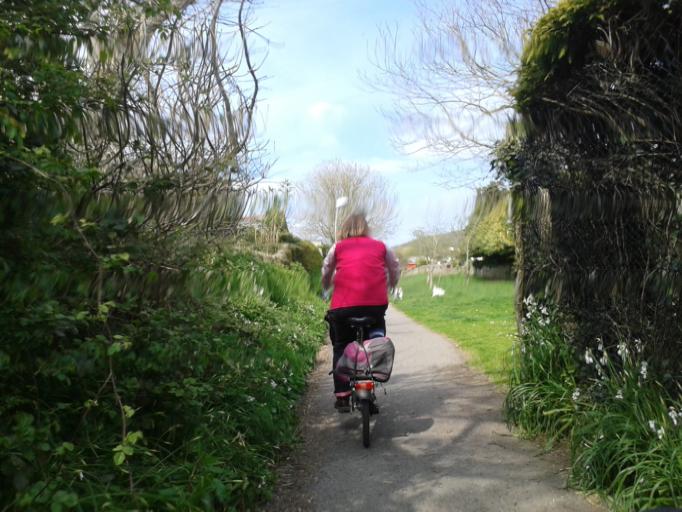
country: GB
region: England
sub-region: Devon
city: Braunton
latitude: 51.1110
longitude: -4.1626
